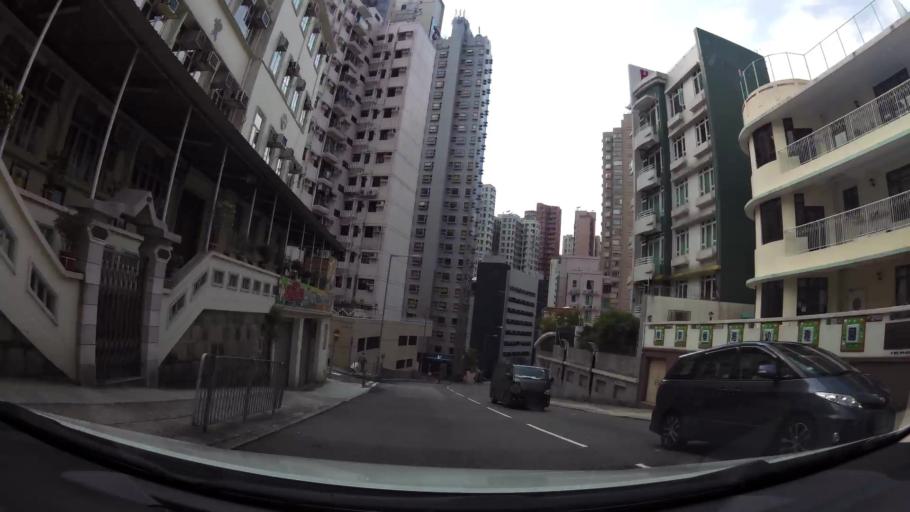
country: HK
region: Wanchai
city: Wan Chai
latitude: 22.2665
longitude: 114.1881
